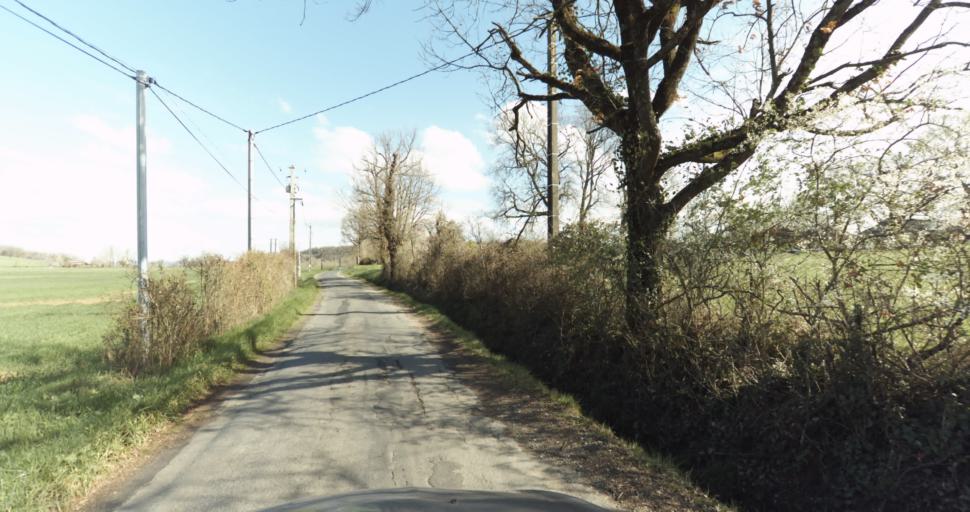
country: FR
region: Midi-Pyrenees
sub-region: Departement du Tarn
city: Puygouzon
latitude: 43.8876
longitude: 2.1845
